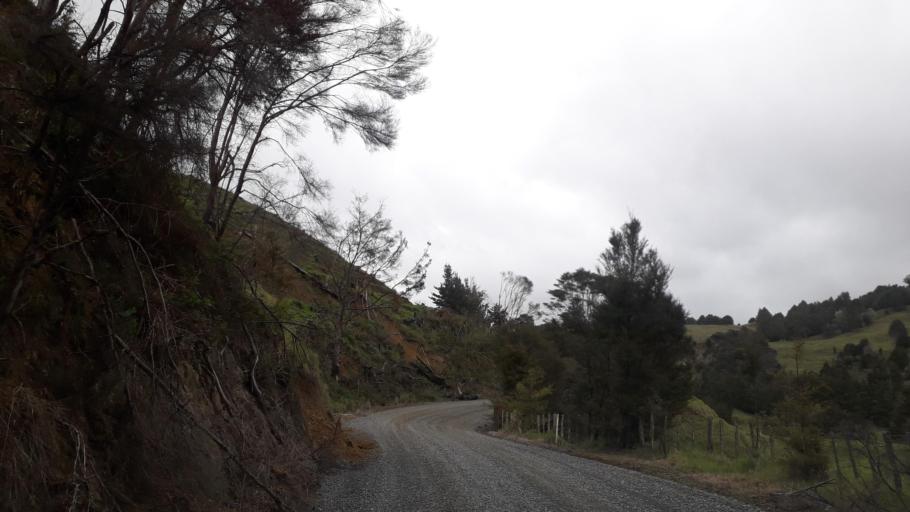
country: NZ
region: Northland
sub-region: Far North District
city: Kerikeri
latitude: -35.1306
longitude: 173.7194
